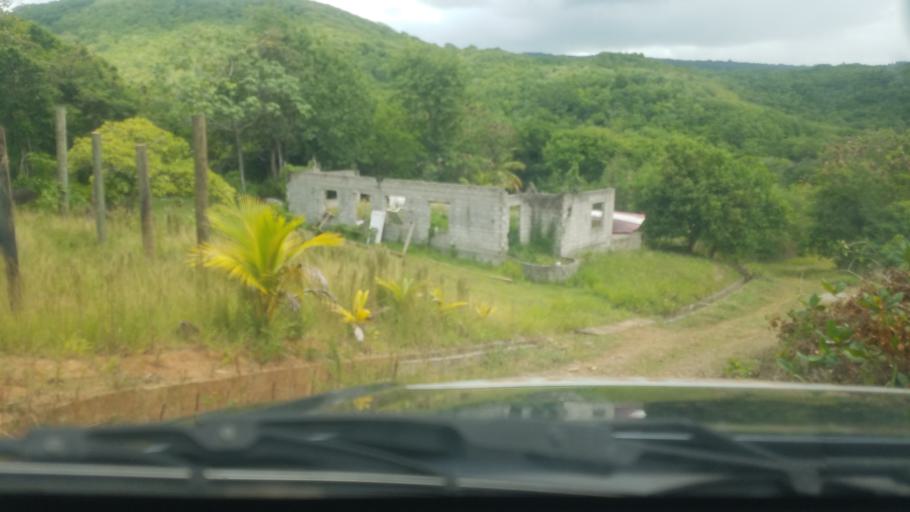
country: LC
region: Praslin
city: Praslin
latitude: 13.8642
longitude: -60.9019
